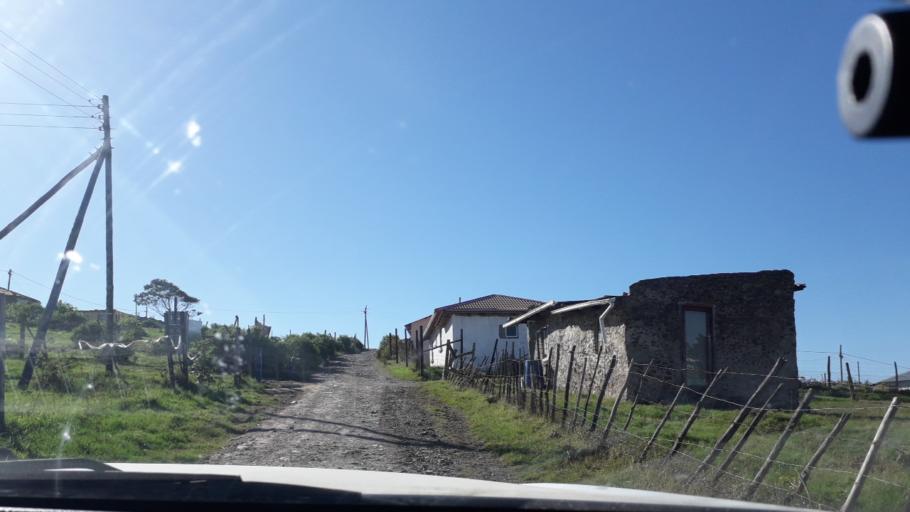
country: ZA
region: Eastern Cape
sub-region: Buffalo City Metropolitan Municipality
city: East London
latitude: -32.8455
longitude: 27.9857
